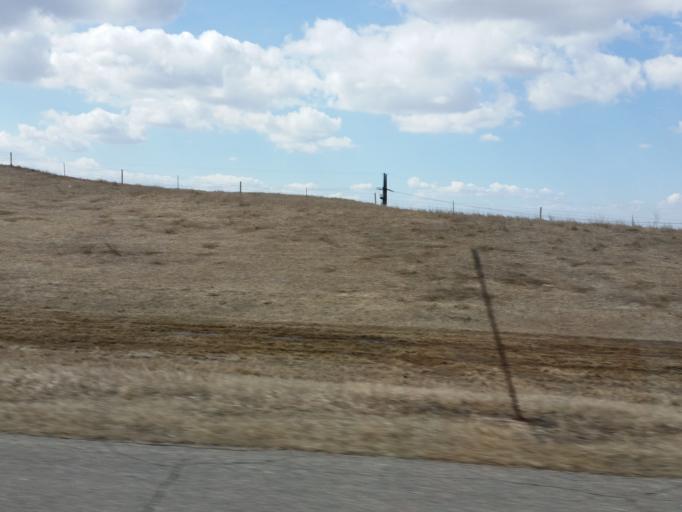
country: US
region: South Dakota
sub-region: Roberts County
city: Sisseton
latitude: 45.3243
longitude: -97.0515
